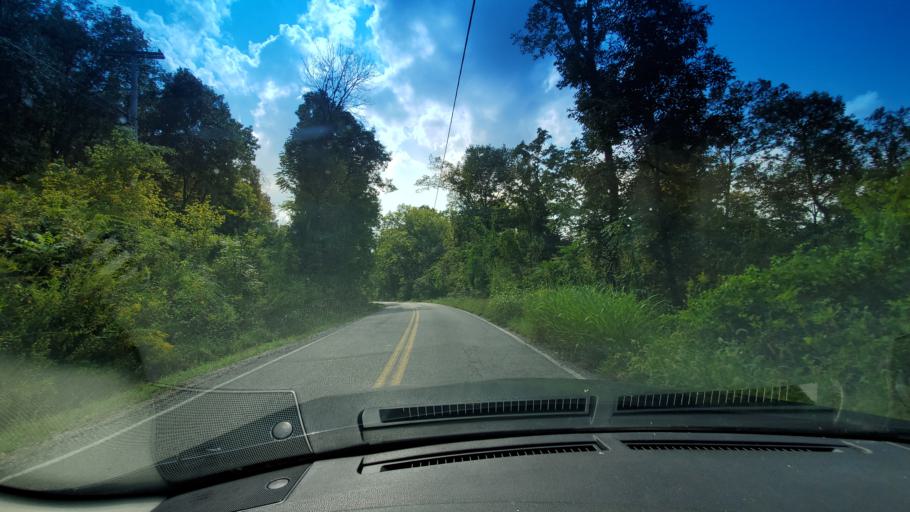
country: US
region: Tennessee
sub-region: Smith County
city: South Carthage
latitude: 36.2456
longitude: -85.9676
